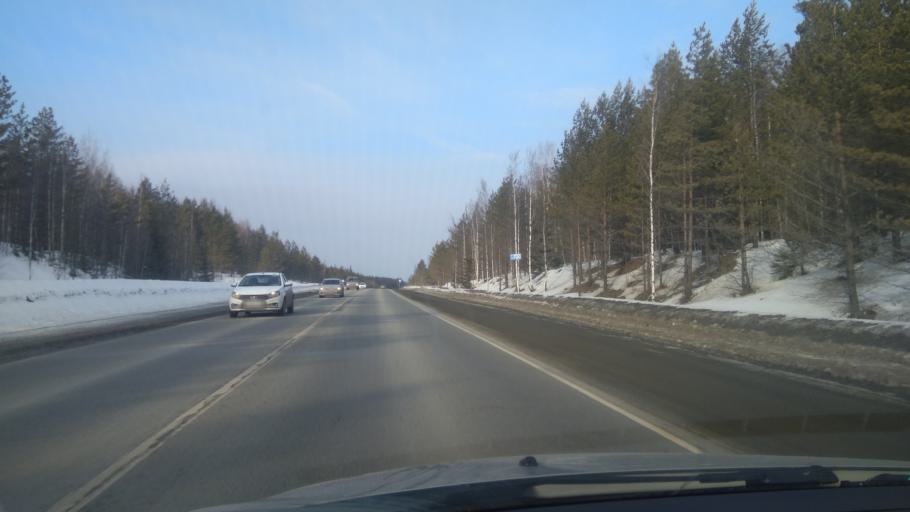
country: RU
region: Sverdlovsk
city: Nizhniye Sergi
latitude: 56.8250
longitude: 59.2465
